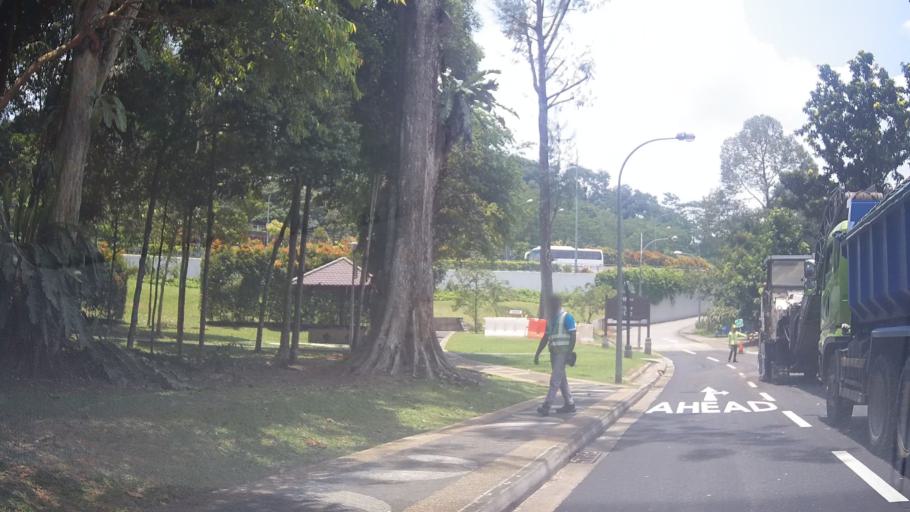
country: SG
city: Singapore
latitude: 1.3416
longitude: 103.7816
